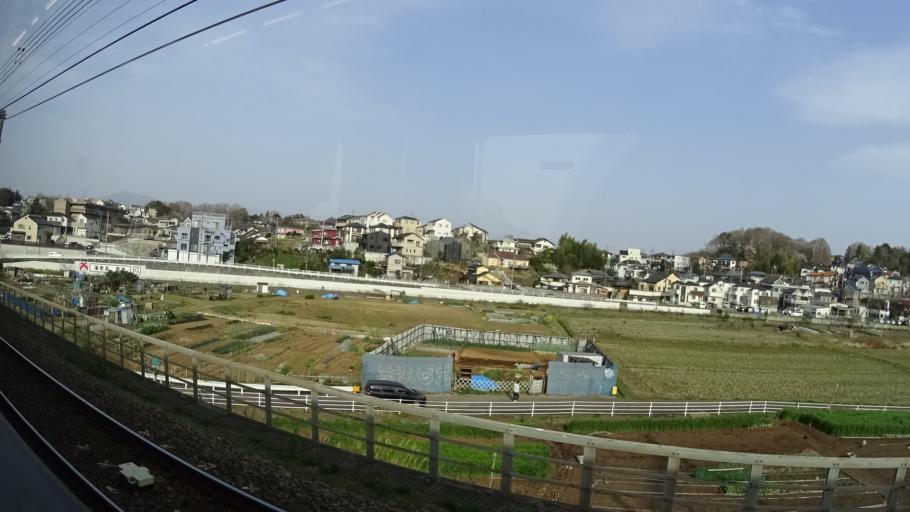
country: JP
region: Kanagawa
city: Zama
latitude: 35.4603
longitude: 139.4069
